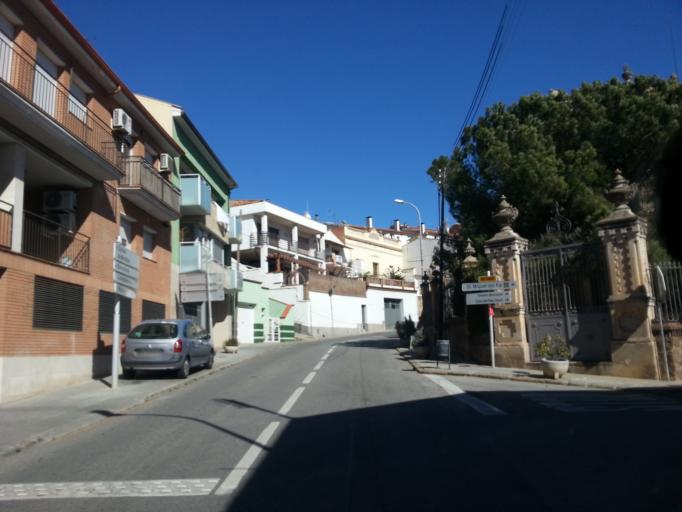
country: ES
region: Catalonia
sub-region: Provincia de Barcelona
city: Sant Feliu de Codines
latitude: 41.6892
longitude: 2.1661
